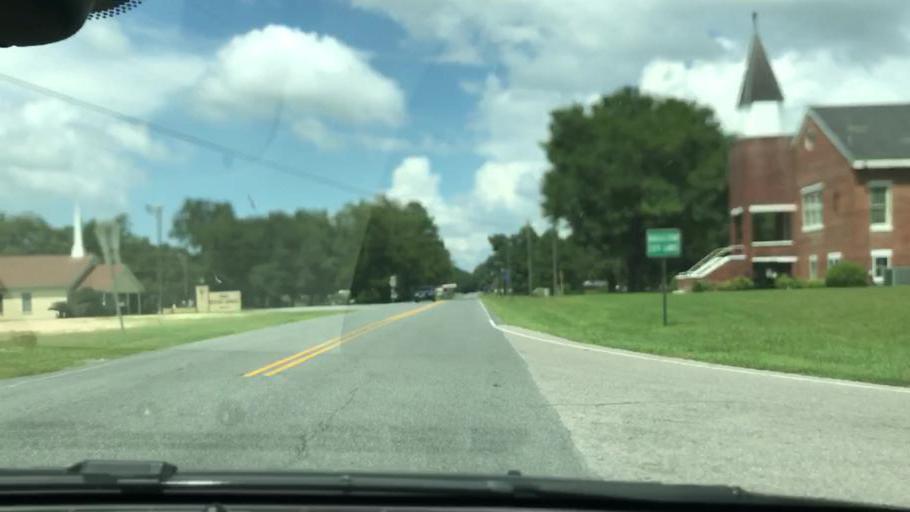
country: US
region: Florida
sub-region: Jackson County
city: Malone
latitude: 30.9223
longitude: -85.1187
